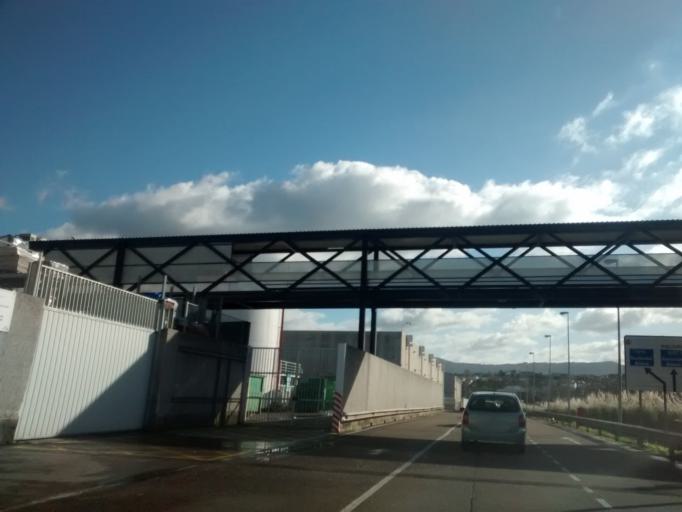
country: ES
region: Cantabria
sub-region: Provincia de Cantabria
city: El Astillero
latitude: 43.4278
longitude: -3.8403
